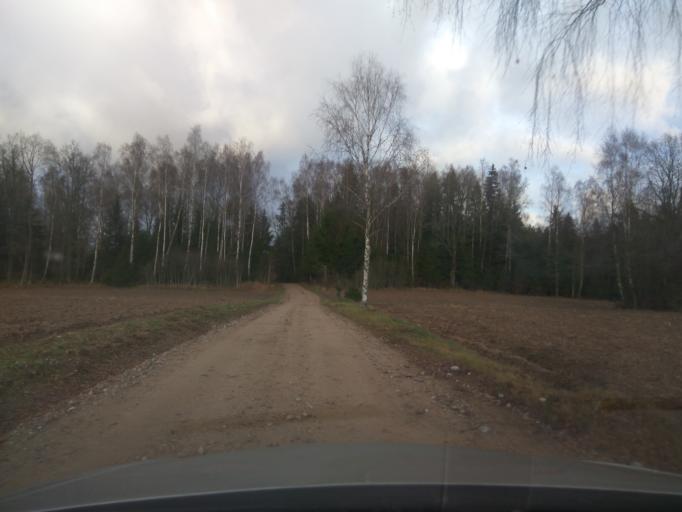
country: LV
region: Kuldigas Rajons
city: Kuldiga
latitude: 56.8330
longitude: 21.8271
